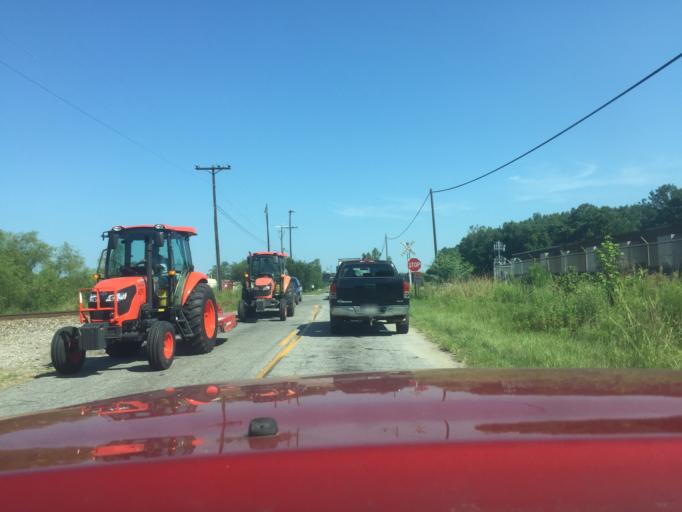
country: US
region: Georgia
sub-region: Chatham County
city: Garden City
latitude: 32.0761
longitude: -81.1440
